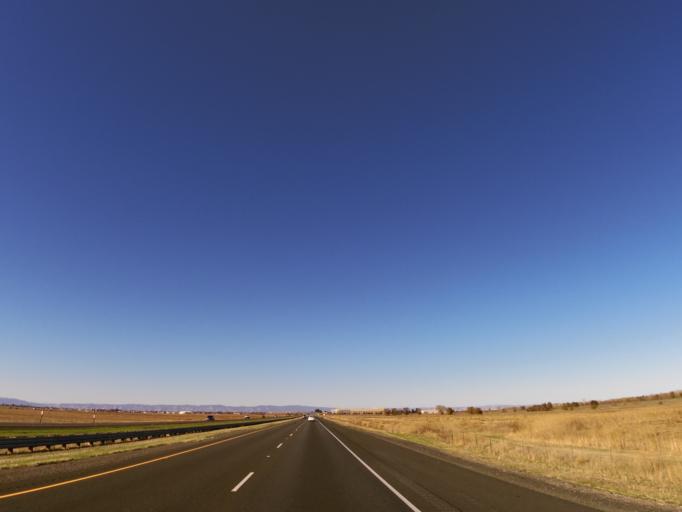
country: US
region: California
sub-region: Yolo County
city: Woodland
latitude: 38.6737
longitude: -121.6928
